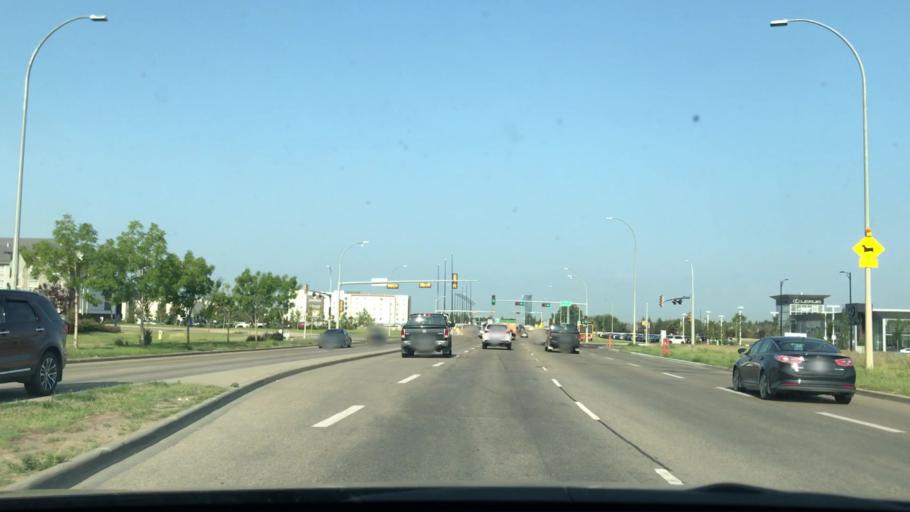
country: CA
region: Alberta
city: Beaumont
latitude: 53.4249
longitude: -113.4874
